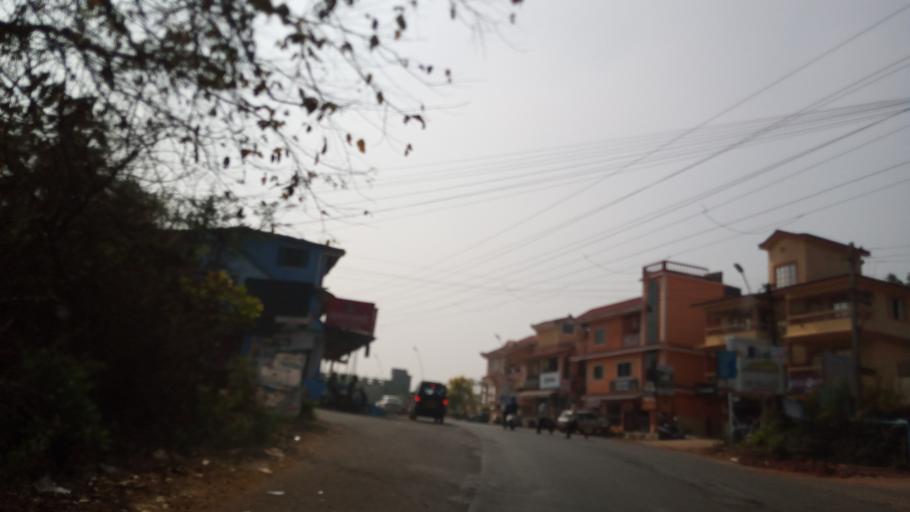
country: IN
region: Goa
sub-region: North Goa
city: Serula
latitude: 15.5402
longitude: 73.8168
